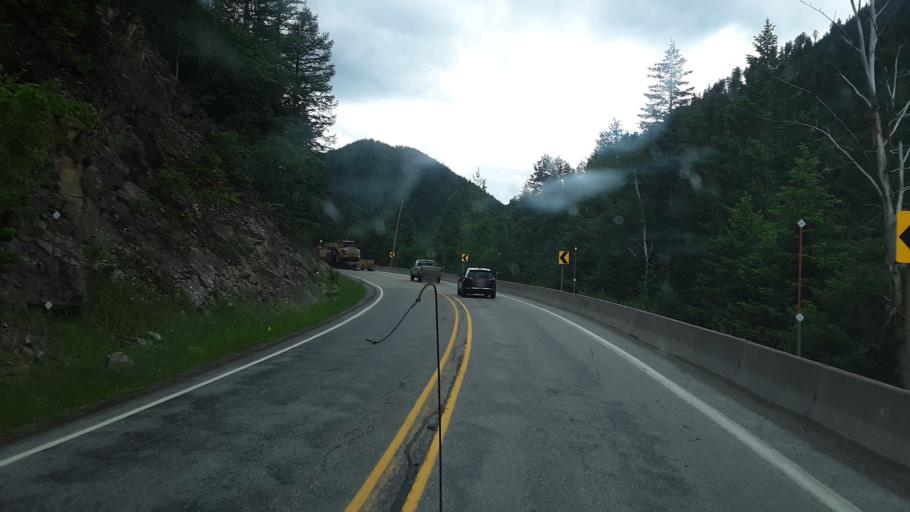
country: US
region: Montana
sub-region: Flathead County
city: Columbia Falls
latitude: 48.5014
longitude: -113.9313
